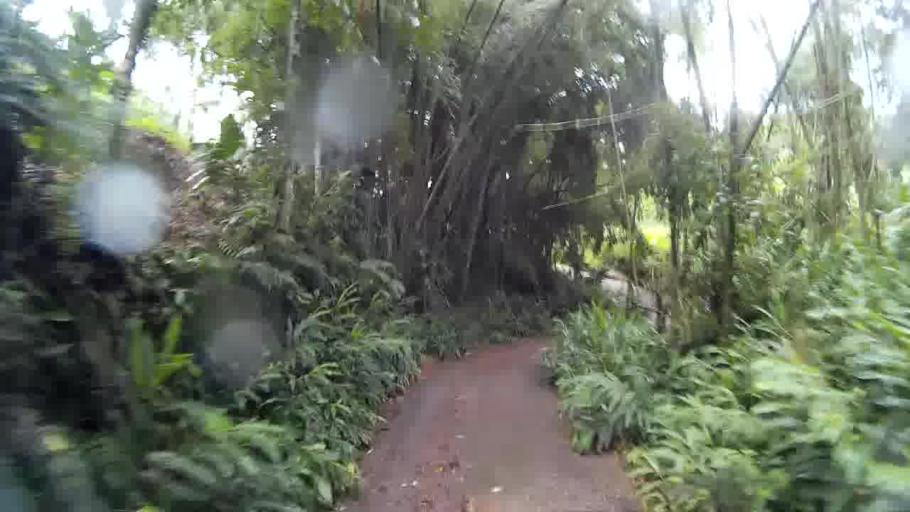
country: CO
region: Quindio
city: Filandia
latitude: 4.7199
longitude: -75.6872
